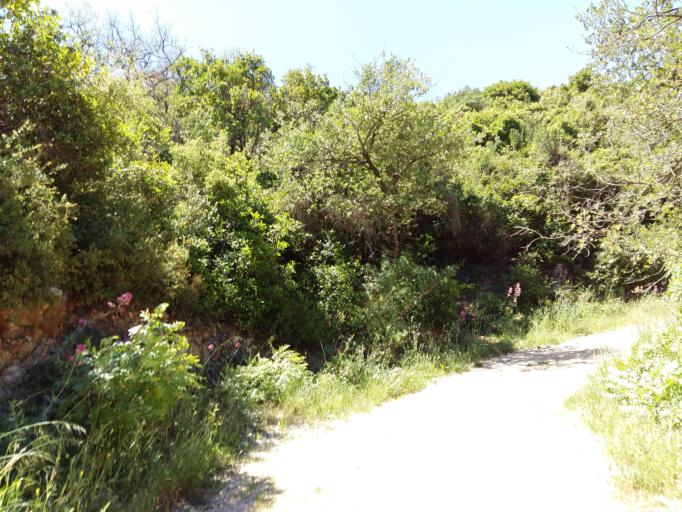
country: FR
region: Provence-Alpes-Cote d'Azur
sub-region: Departement des Bouches-du-Rhone
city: Marseille 11
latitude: 43.2833
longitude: 5.4729
